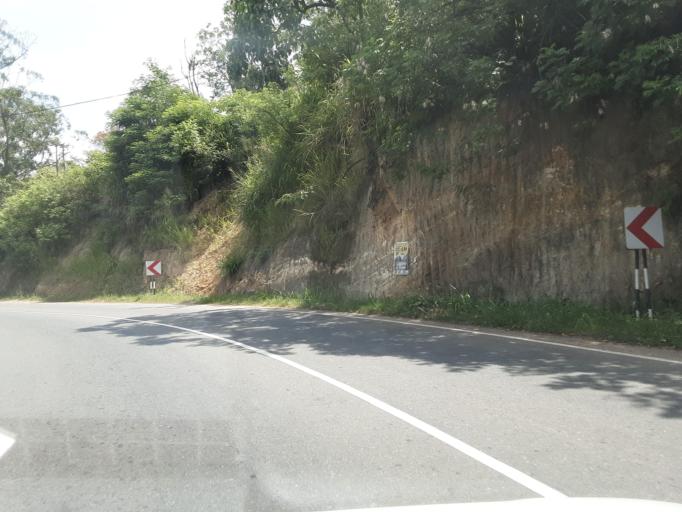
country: LK
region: Central
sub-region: Nuwara Eliya District
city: Nuwara Eliya
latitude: 6.9245
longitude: 80.8985
